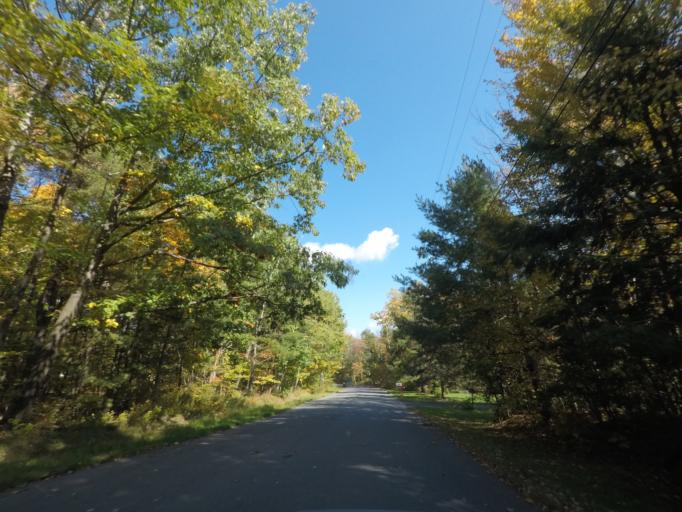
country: US
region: New York
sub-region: Rensselaer County
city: Averill Park
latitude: 42.6458
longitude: -73.5528
